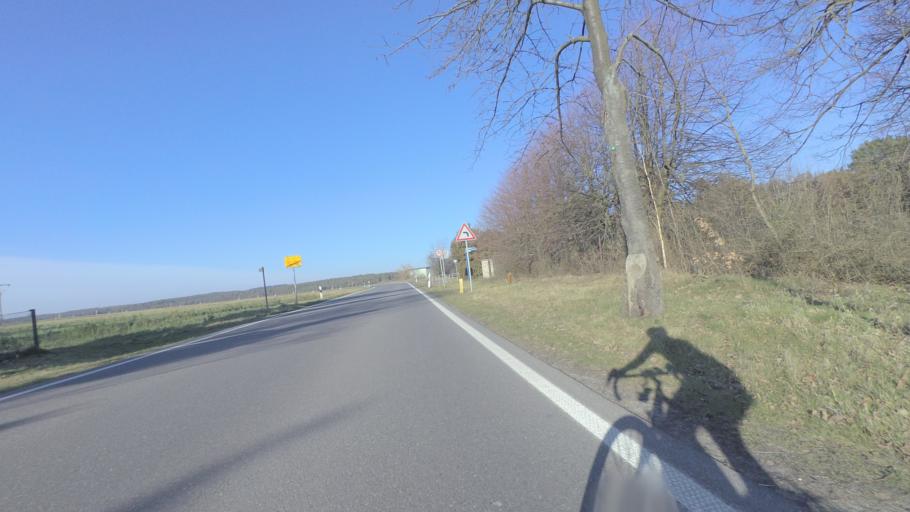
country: DE
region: Brandenburg
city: Ihlow
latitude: 51.9906
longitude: 13.3565
